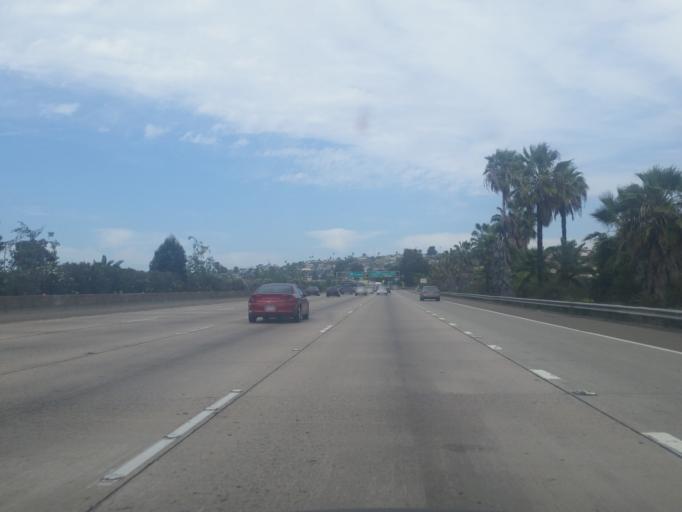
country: US
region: California
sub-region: San Diego County
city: San Diego
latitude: 32.7847
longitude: -117.2074
